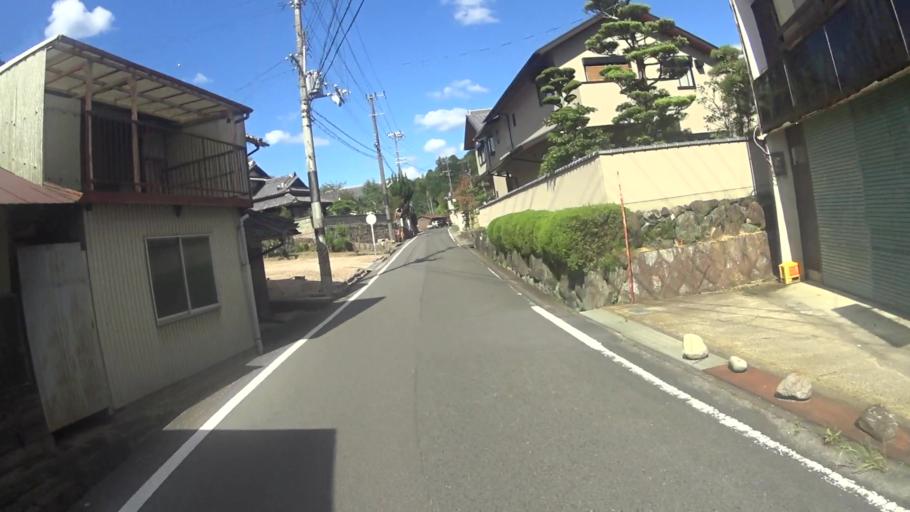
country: JP
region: Mie
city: Ueno-ebisumachi
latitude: 34.7404
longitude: 136.0211
